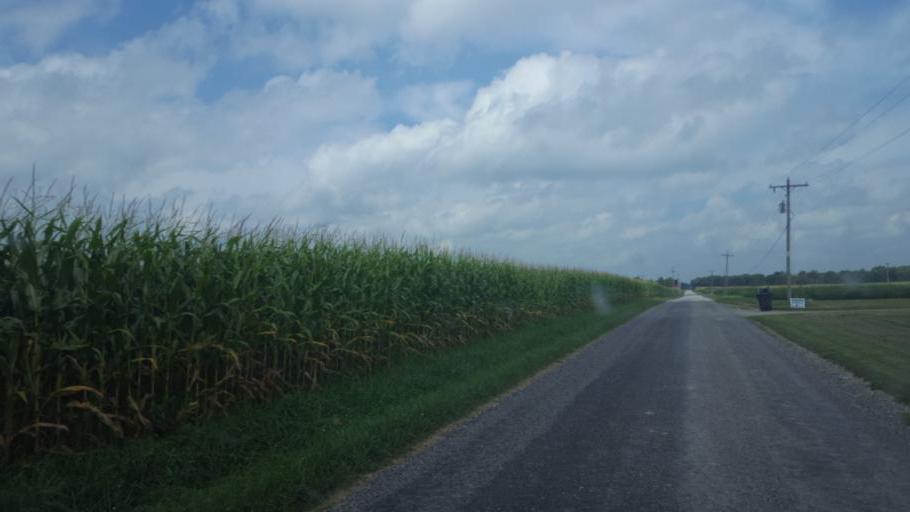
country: US
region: Ohio
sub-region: Crawford County
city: Galion
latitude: 40.6213
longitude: -82.7091
